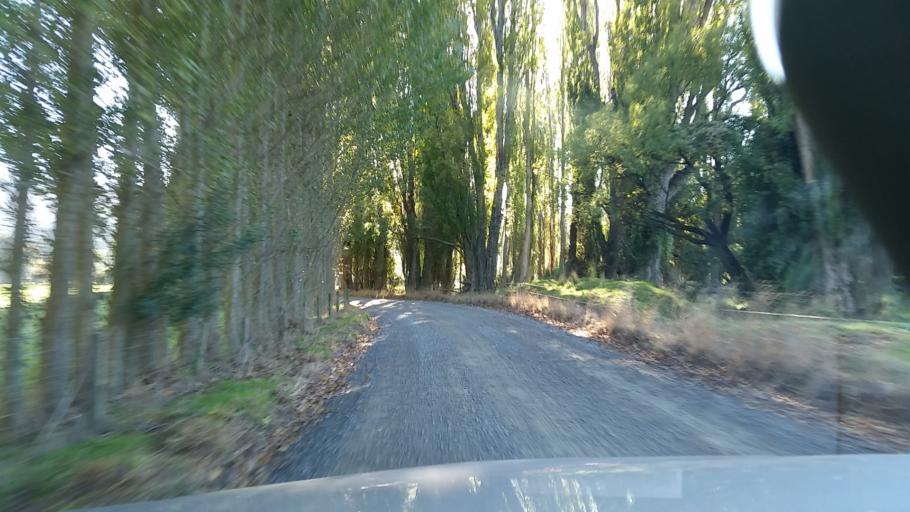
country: NZ
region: Marlborough
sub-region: Marlborough District
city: Blenheim
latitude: -41.4448
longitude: 173.8955
